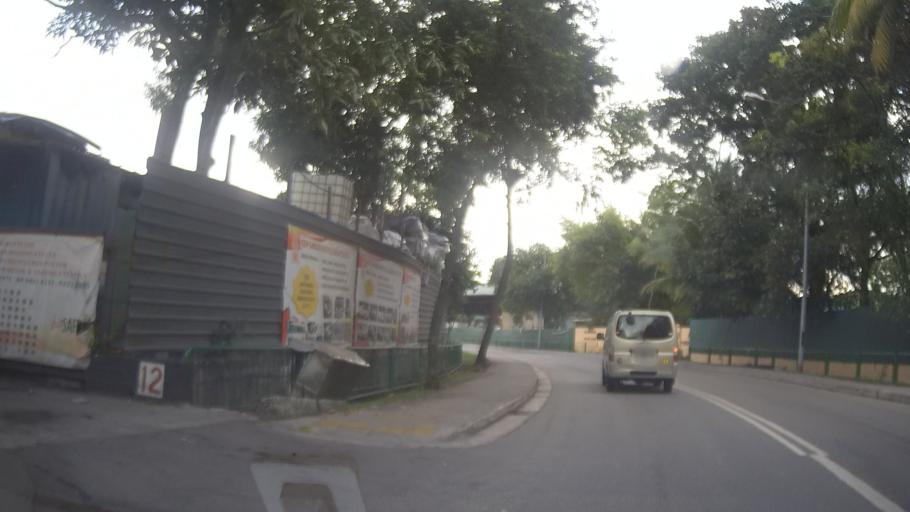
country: MY
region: Johor
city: Johor Bahru
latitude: 1.4211
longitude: 103.7456
